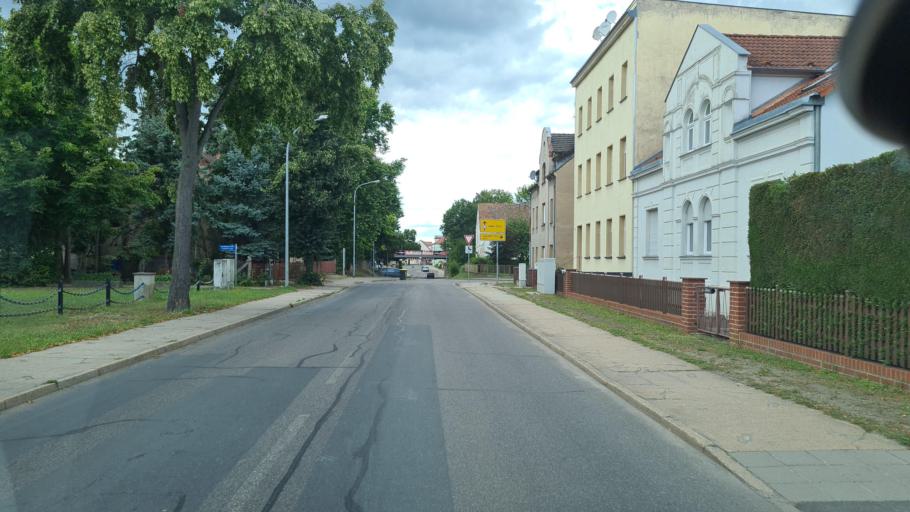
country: DE
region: Brandenburg
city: Drebkau
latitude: 51.6550
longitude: 14.2262
